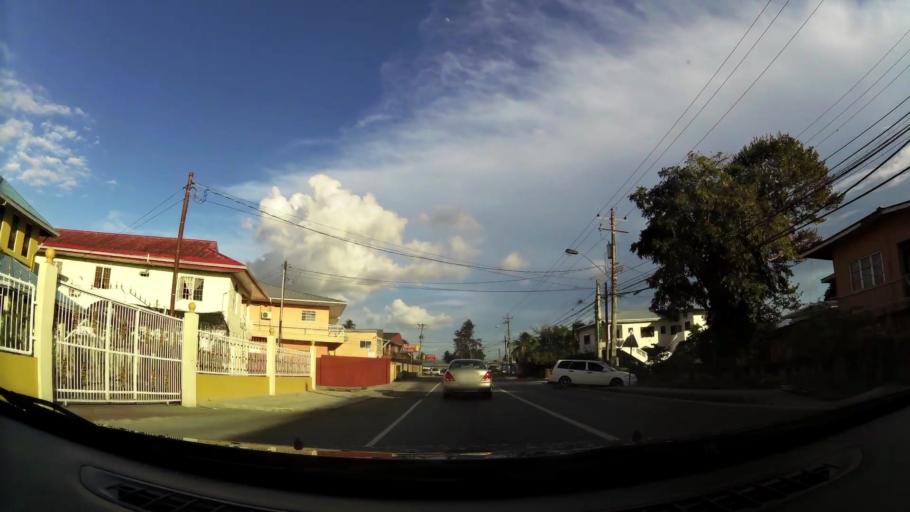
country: TT
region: Tunapuna/Piarco
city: Tunapuna
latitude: 10.5903
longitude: -61.3648
